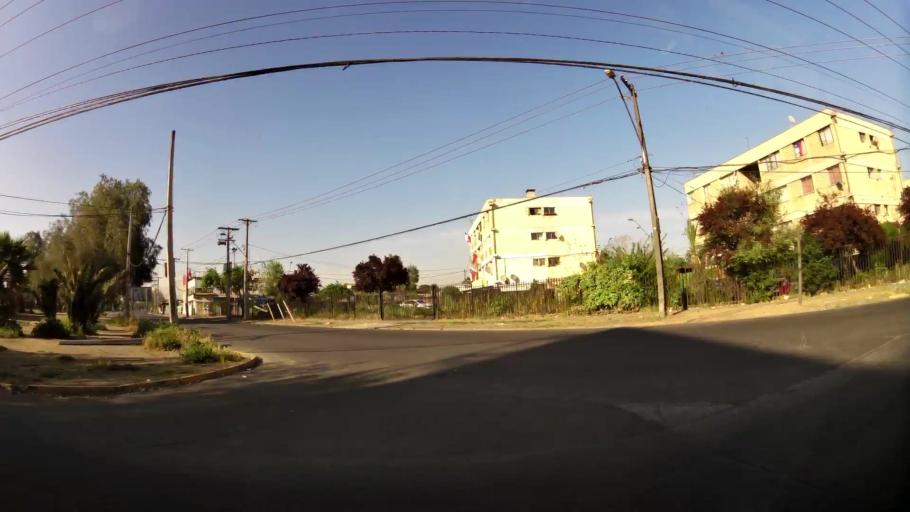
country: CL
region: Santiago Metropolitan
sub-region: Provincia de Santiago
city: Santiago
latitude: -33.3752
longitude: -70.6621
